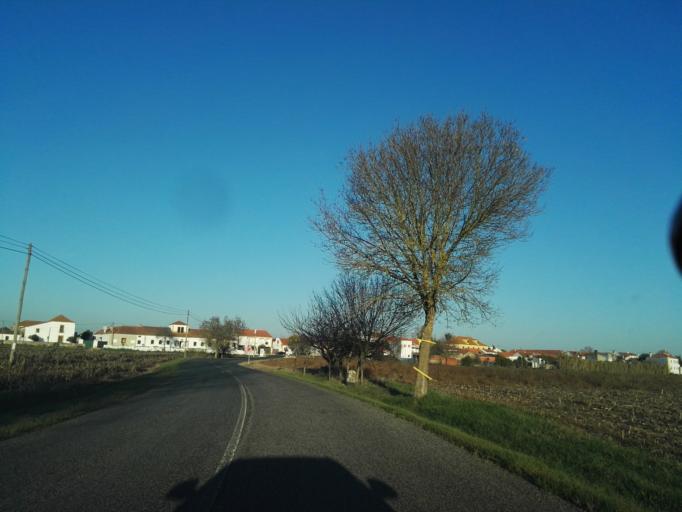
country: PT
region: Santarem
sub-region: Alpiarca
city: Alpiarca
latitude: 39.3414
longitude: -8.5600
